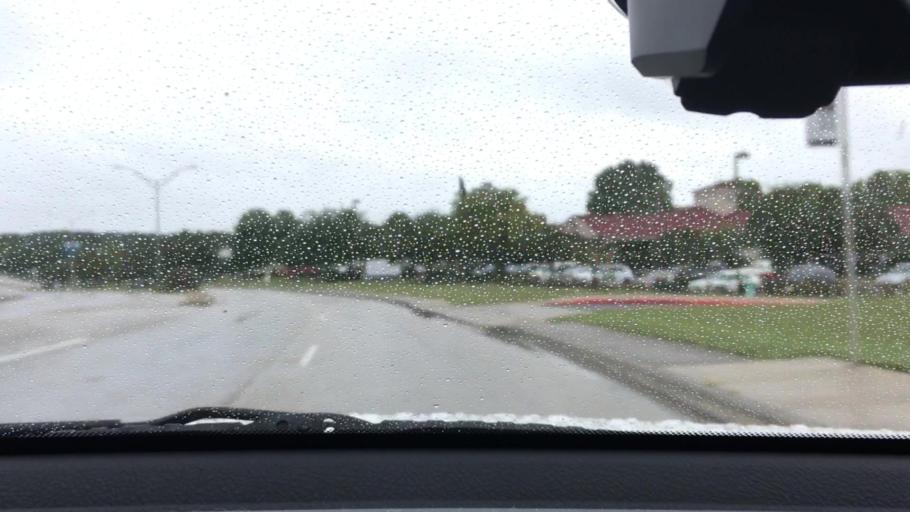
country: US
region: Texas
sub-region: Bexar County
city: Leon Valley
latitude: 29.5265
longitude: -98.5910
